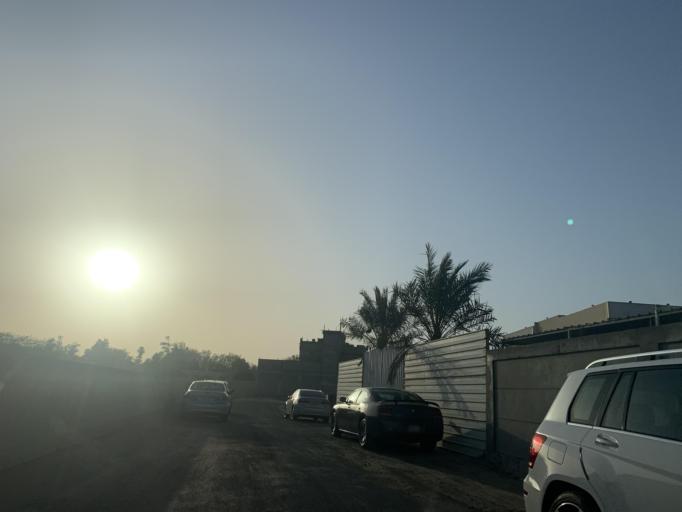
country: BH
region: Manama
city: Jidd Hafs
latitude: 26.2205
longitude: 50.5325
